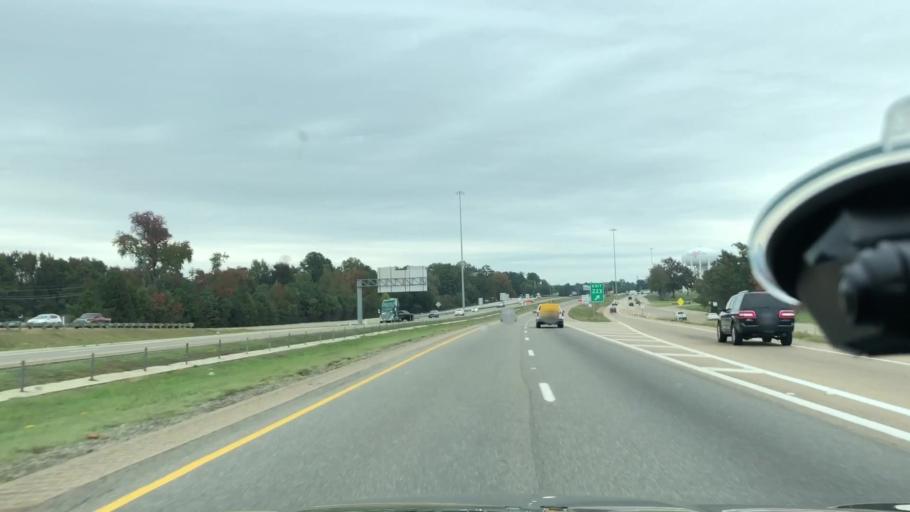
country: US
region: Arkansas
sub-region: Miller County
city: Texarkana
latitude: 33.4674
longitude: -94.0619
